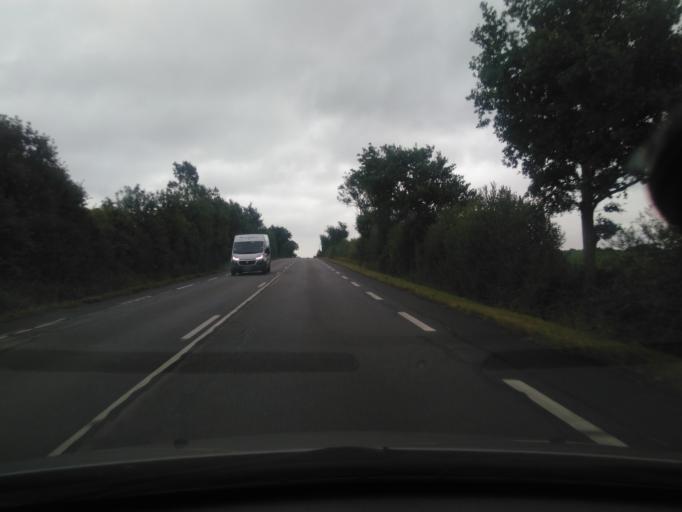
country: FR
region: Pays de la Loire
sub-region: Departement de la Vendee
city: Saint-Florent-des-Bois
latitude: 46.5844
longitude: -1.3016
